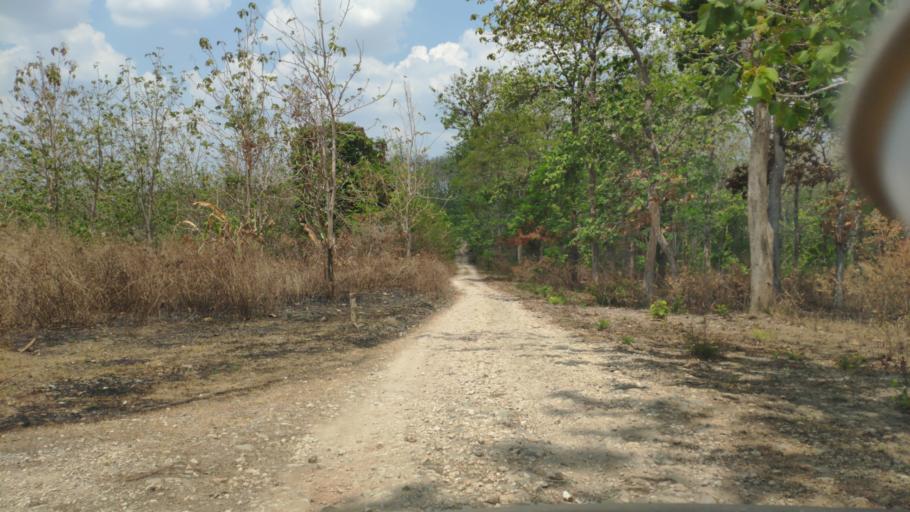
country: ID
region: Central Java
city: Suruhan
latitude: -6.9961
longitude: 111.5252
